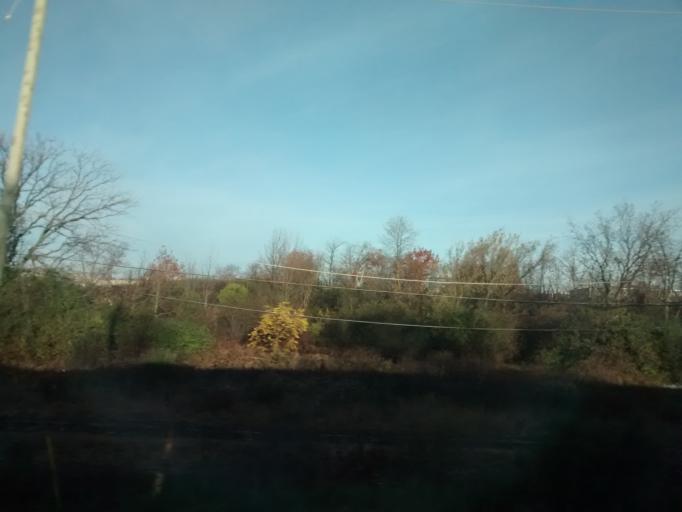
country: CA
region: Ontario
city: Oakville
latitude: 43.4266
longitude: -79.7120
